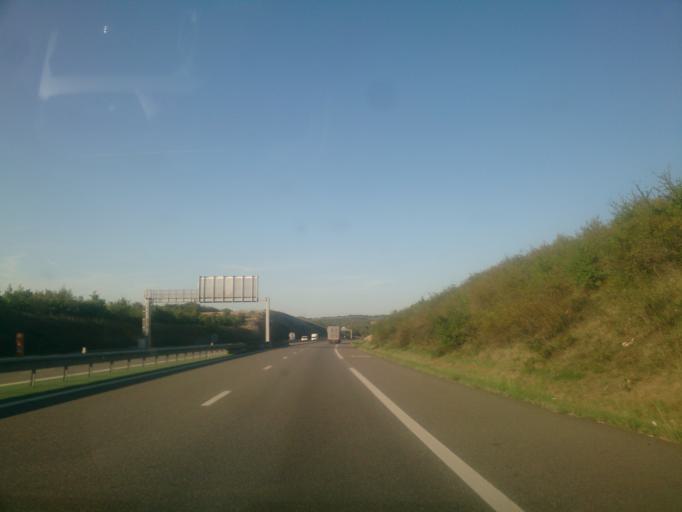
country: FR
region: Midi-Pyrenees
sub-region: Departement du Lot
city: Cahors
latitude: 44.5032
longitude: 1.4959
